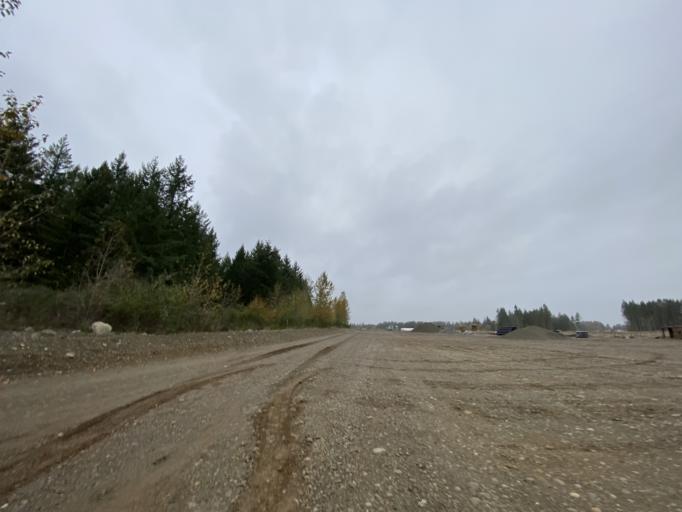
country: US
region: Washington
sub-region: Pierce County
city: Orting
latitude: 47.0905
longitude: -122.2559
